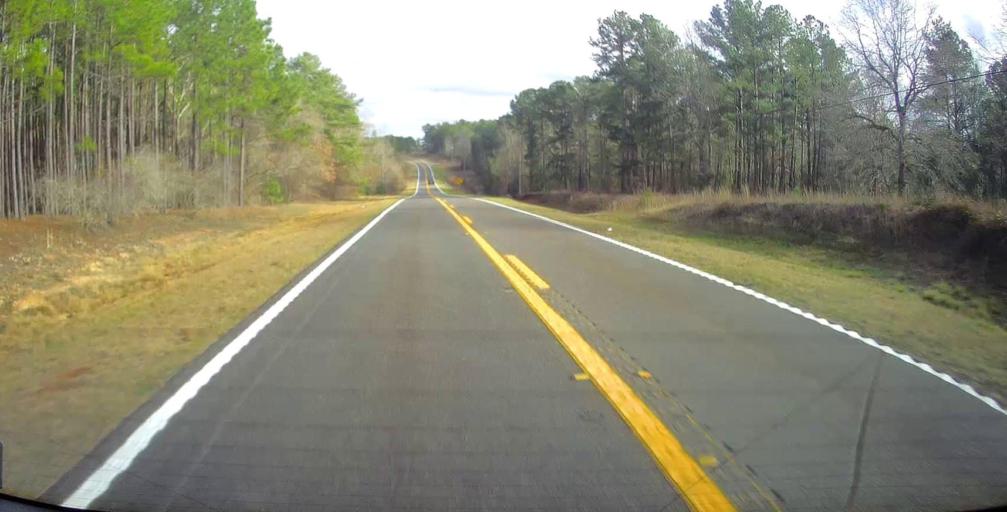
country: US
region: Georgia
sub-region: Marion County
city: Buena Vista
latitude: 32.4404
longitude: -84.5114
